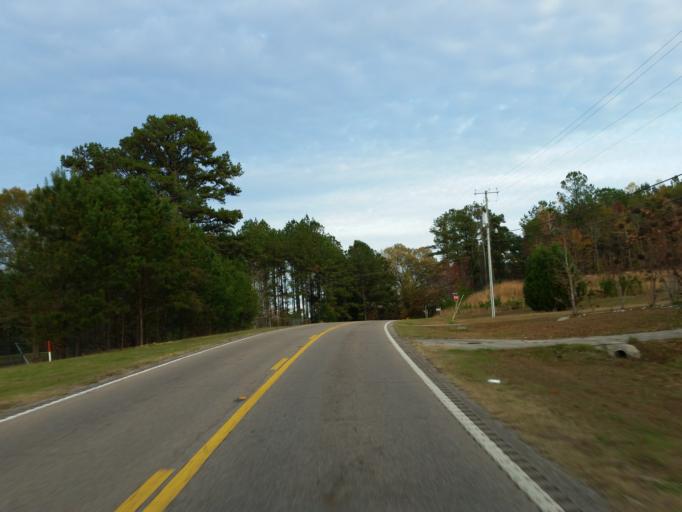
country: US
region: Mississippi
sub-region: Lauderdale County
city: Marion
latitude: 32.4113
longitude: -88.5727
